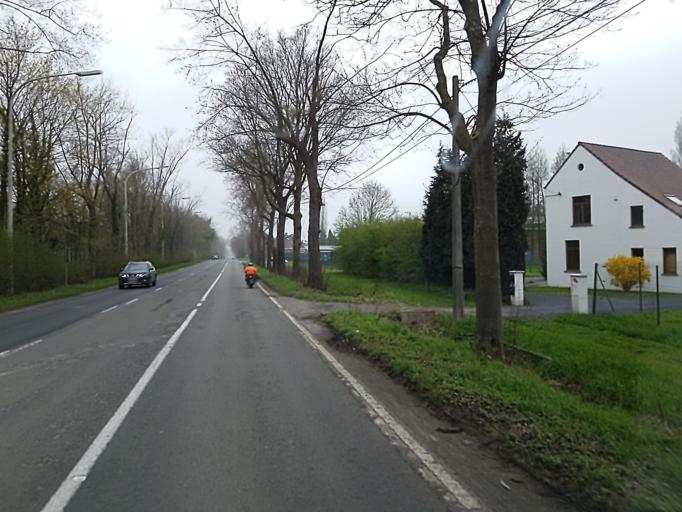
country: BE
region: Wallonia
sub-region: Province du Hainaut
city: Mons
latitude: 50.4776
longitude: 3.9232
